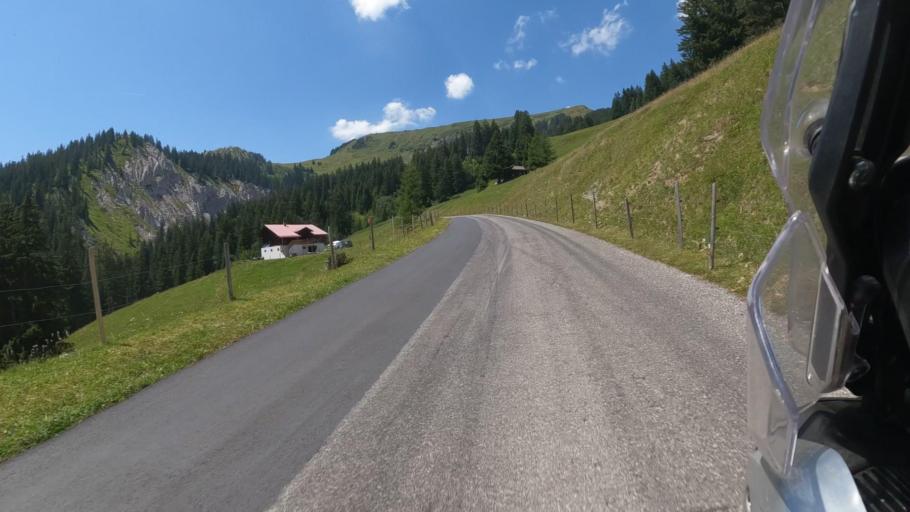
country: CH
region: Vaud
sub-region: Aigle District
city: Villars-sur-Ollon
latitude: 46.3292
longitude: 7.1372
